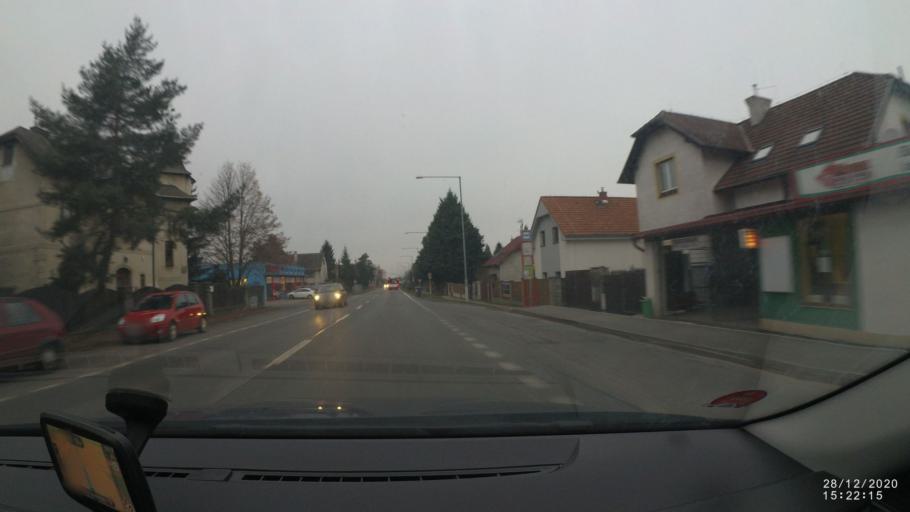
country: CZ
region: Central Bohemia
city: Sestajovice
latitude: 50.0768
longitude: 14.6572
